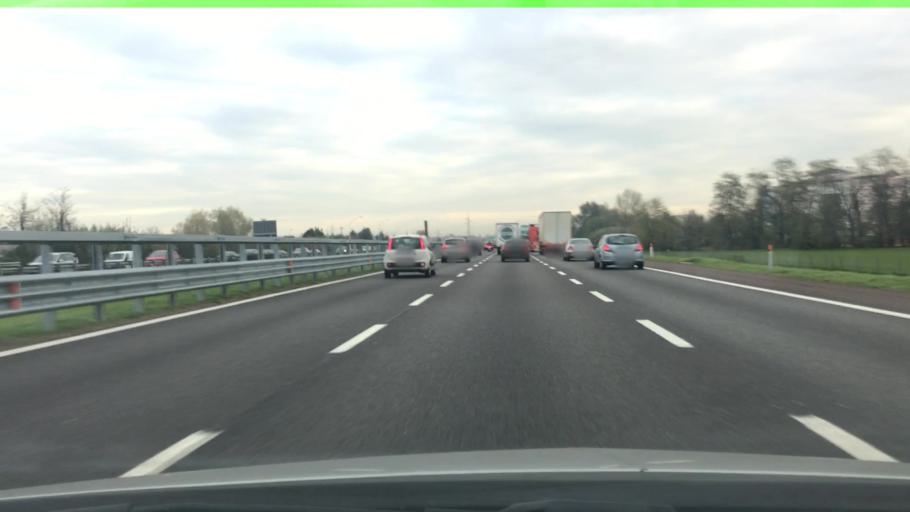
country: IT
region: Lombardy
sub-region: Citta metropolitana di Milano
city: Vimodrone
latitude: 45.5023
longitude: 9.2571
